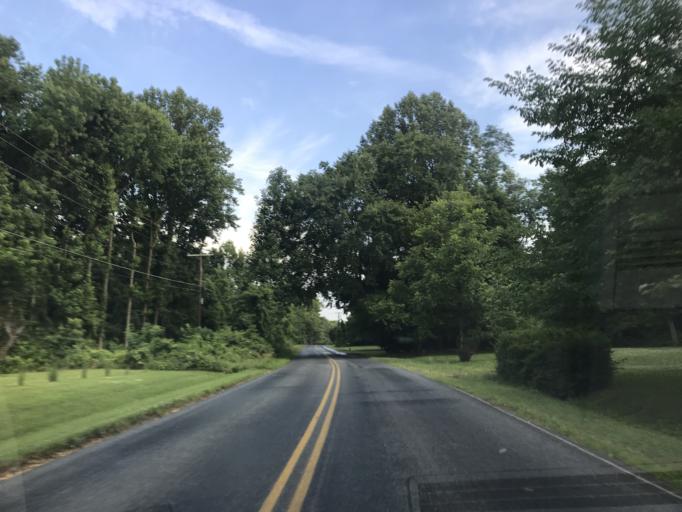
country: US
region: Maryland
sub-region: Harford County
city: Perryman
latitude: 39.5082
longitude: -76.2067
